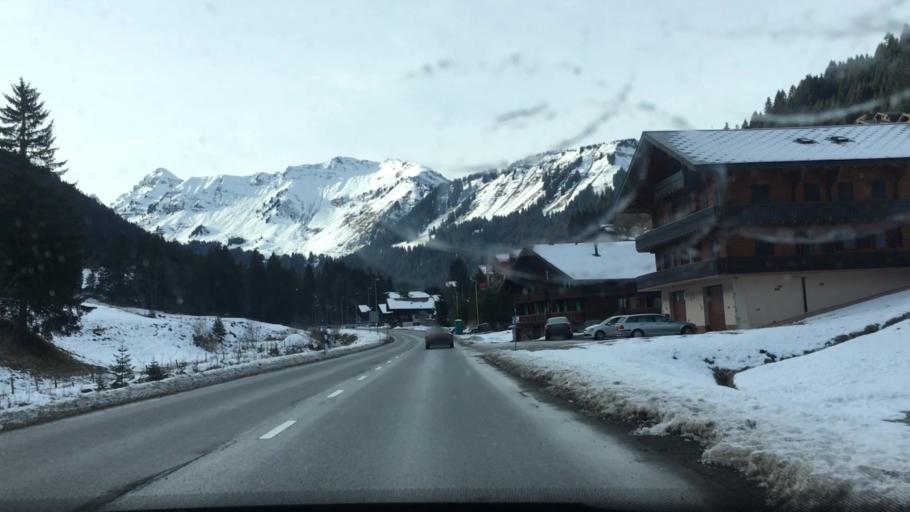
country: FR
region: Rhone-Alpes
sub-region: Departement de la Haute-Savoie
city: Chatel
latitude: 46.2401
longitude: 6.8749
